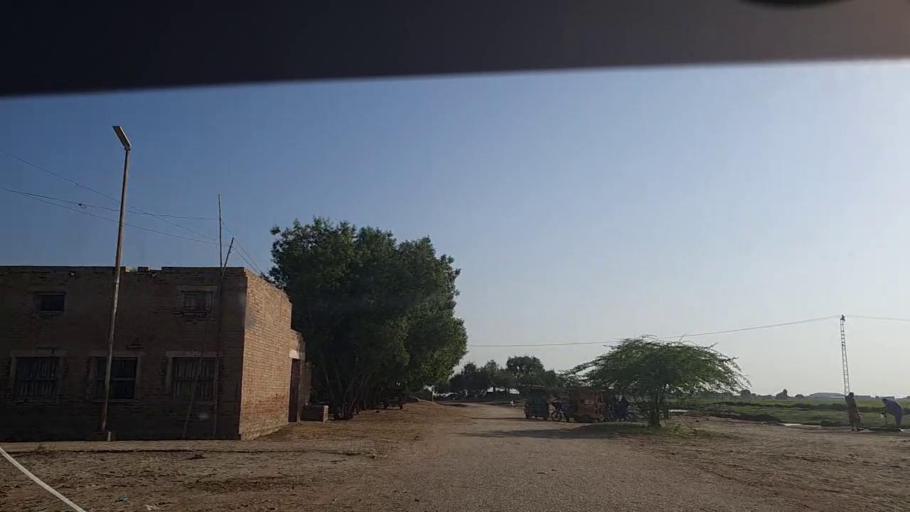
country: PK
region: Sindh
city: Tangwani
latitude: 28.2643
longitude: 69.0144
